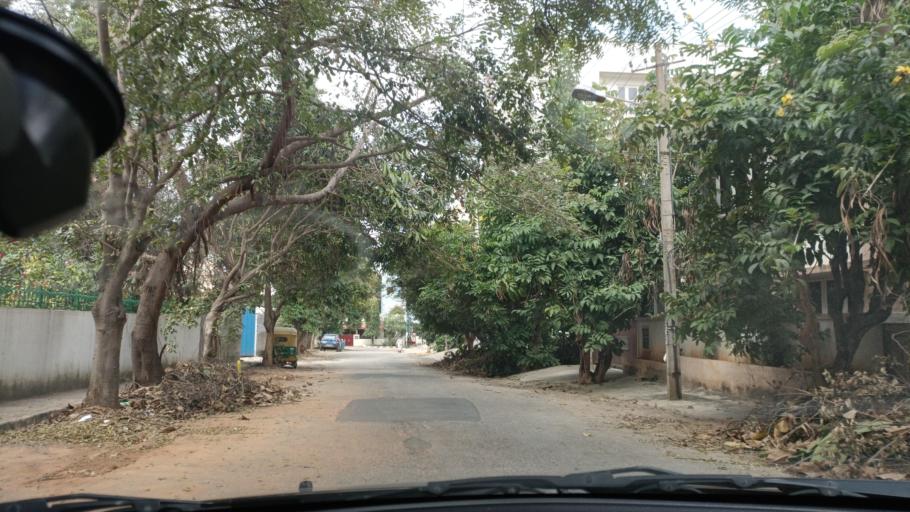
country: IN
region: Karnataka
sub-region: Bangalore Urban
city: Bangalore
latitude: 13.0312
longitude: 77.6313
